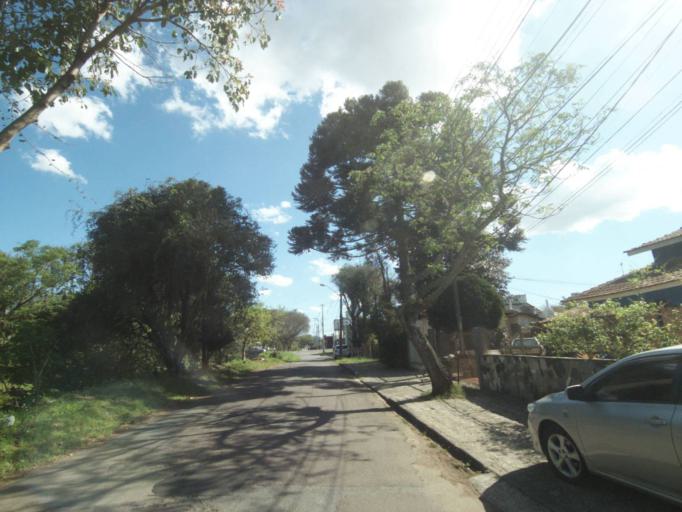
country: BR
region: Parana
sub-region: Curitiba
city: Curitiba
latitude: -25.3864
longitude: -49.2405
